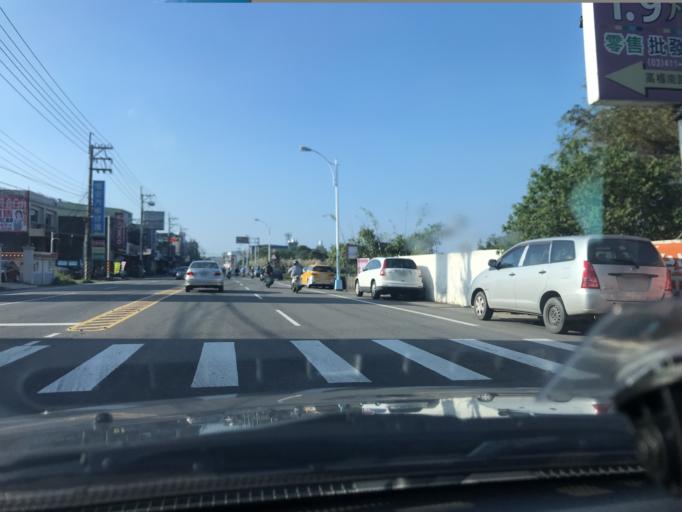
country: TW
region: Taiwan
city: Daxi
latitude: 24.8380
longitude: 121.2089
